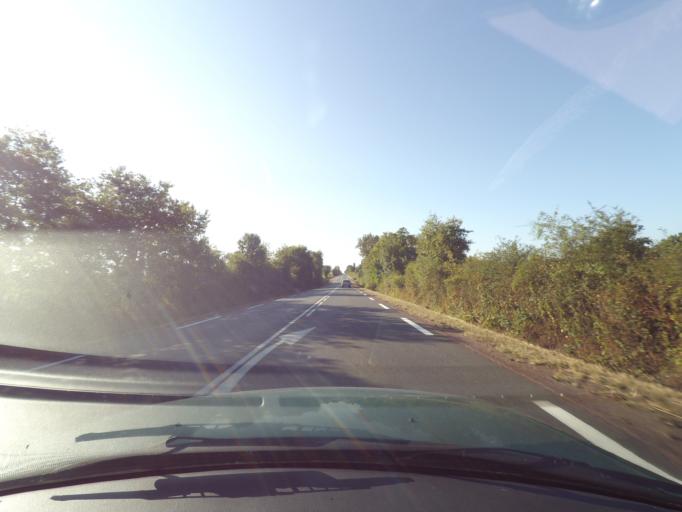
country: FR
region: Poitou-Charentes
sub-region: Departement des Deux-Sevres
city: Viennay
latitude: 46.6808
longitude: -0.2645
